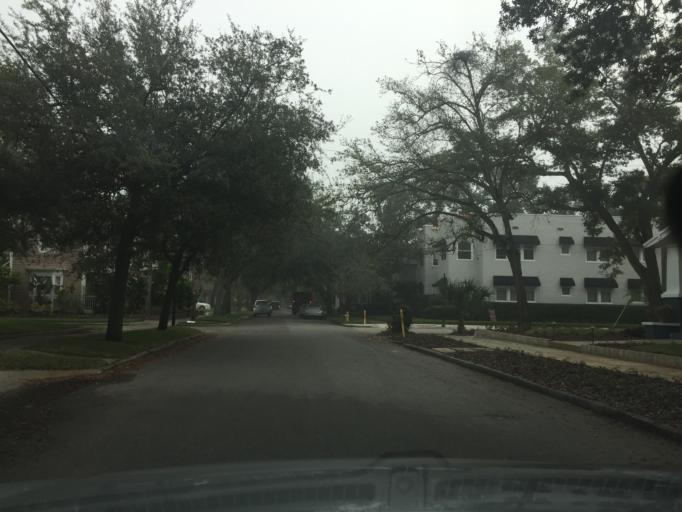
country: US
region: Florida
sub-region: Hillsborough County
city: Tampa
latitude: 27.9329
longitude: -82.4793
